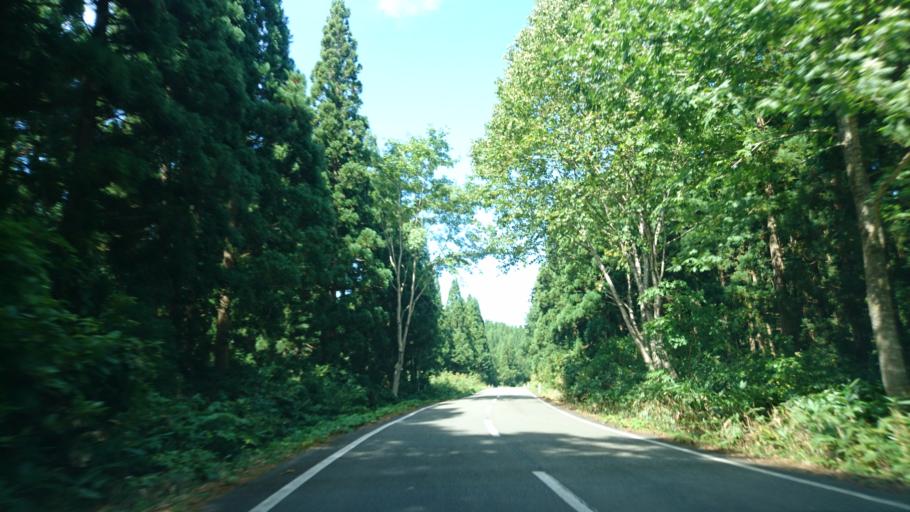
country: JP
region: Akita
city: Yuzawa
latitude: 38.9716
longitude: 140.7115
